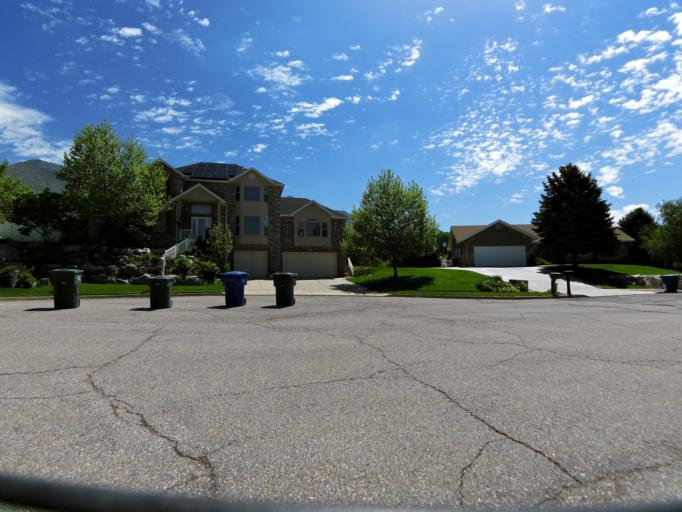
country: US
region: Utah
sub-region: Weber County
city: Washington Terrace
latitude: 41.1726
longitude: -111.9433
